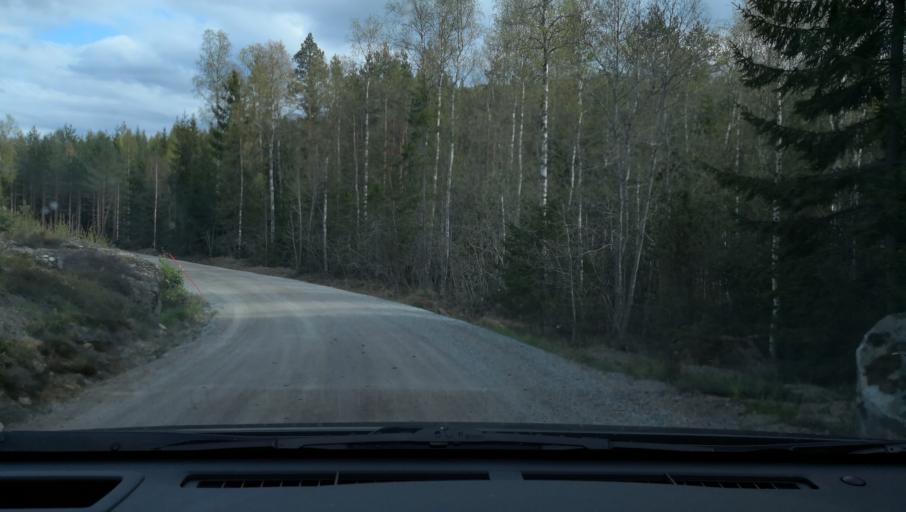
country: SE
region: Vaestmanland
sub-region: Fagersta Kommun
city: Fagersta
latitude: 60.1582
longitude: 15.7074
